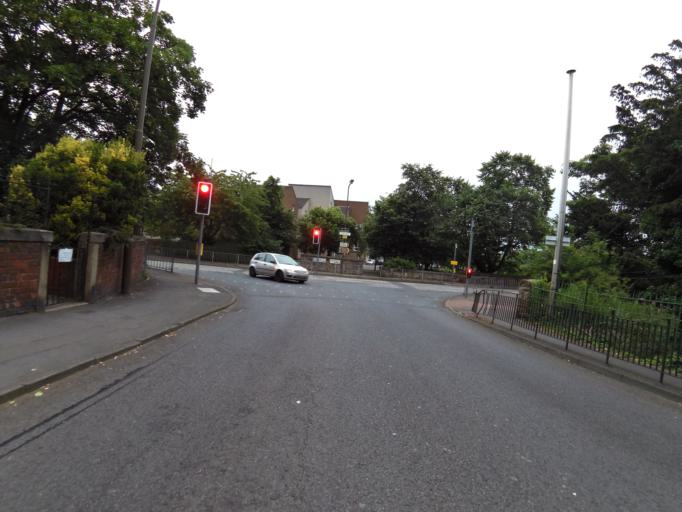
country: GB
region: Scotland
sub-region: East Lothian
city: Musselburgh
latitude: 55.9398
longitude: -3.0608
